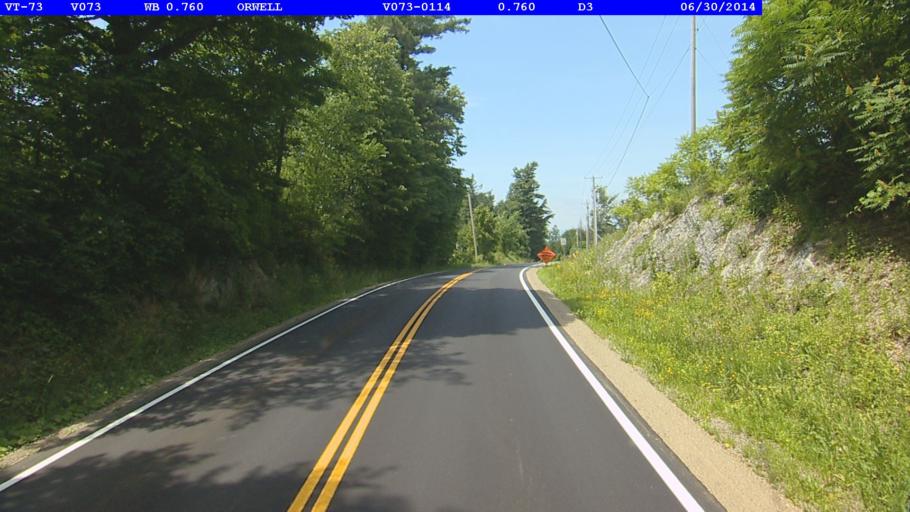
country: US
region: New York
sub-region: Essex County
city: Ticonderoga
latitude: 43.8028
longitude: -73.2906
